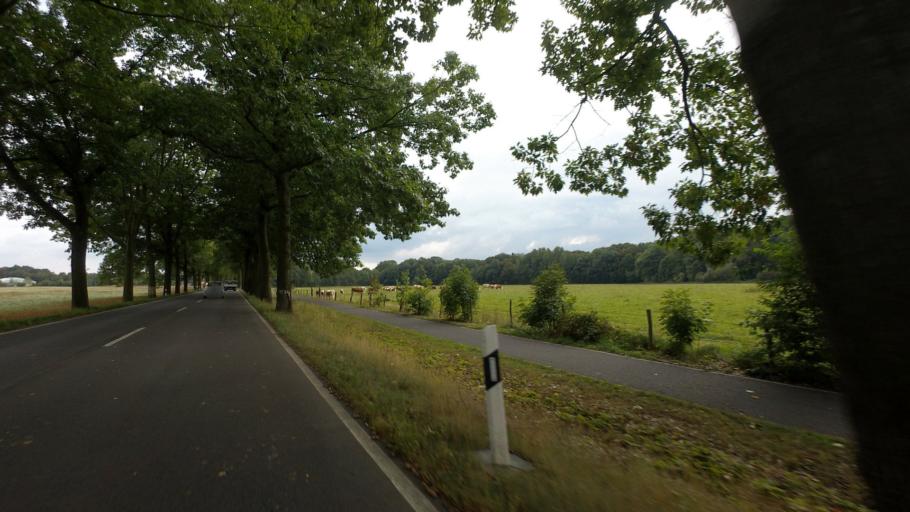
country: DE
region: Saxony
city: Konigswartha
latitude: 51.3577
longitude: 14.3191
